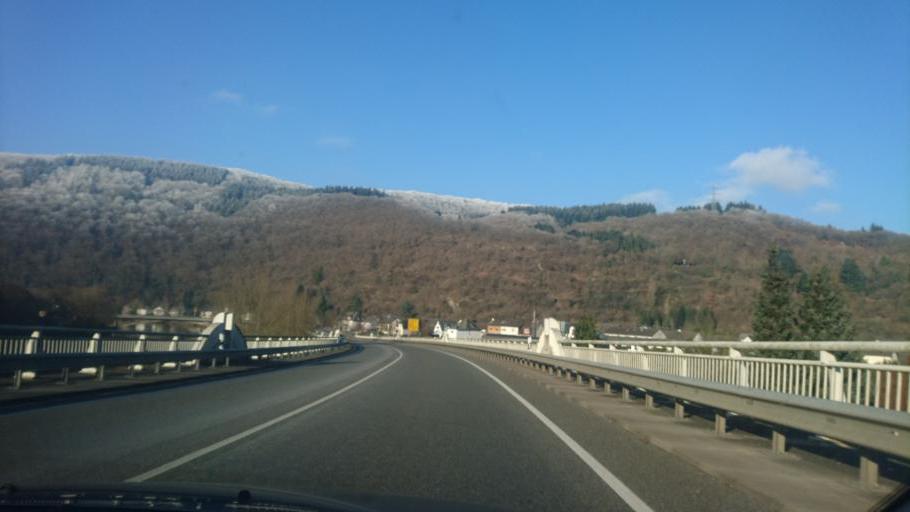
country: DE
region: Rheinland-Pfalz
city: Fachbach
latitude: 50.3368
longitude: 7.6876
